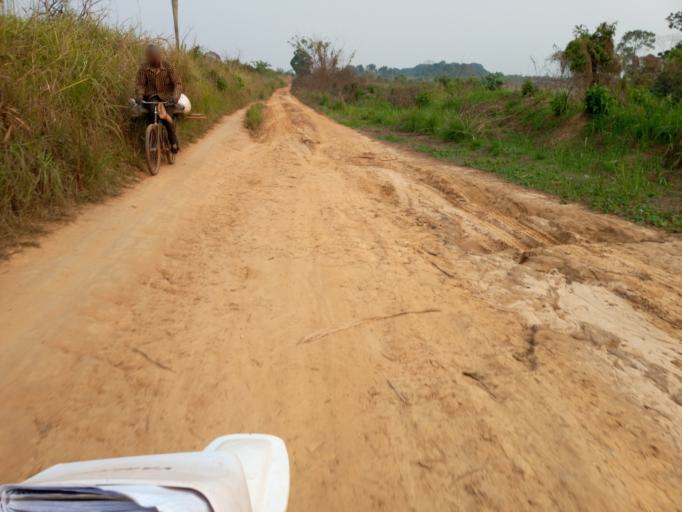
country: CD
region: Bandundu
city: Bandundu
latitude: -3.4430
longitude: 17.6062
